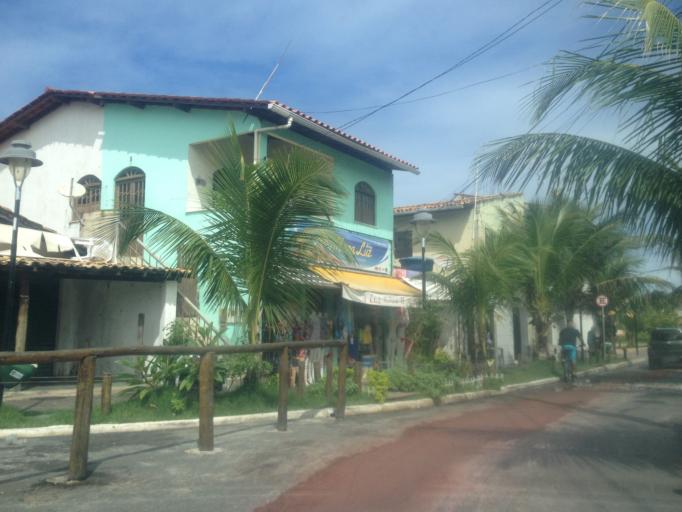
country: BR
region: Bahia
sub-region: Camacari
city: Camacari
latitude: -12.7725
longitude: -38.1762
